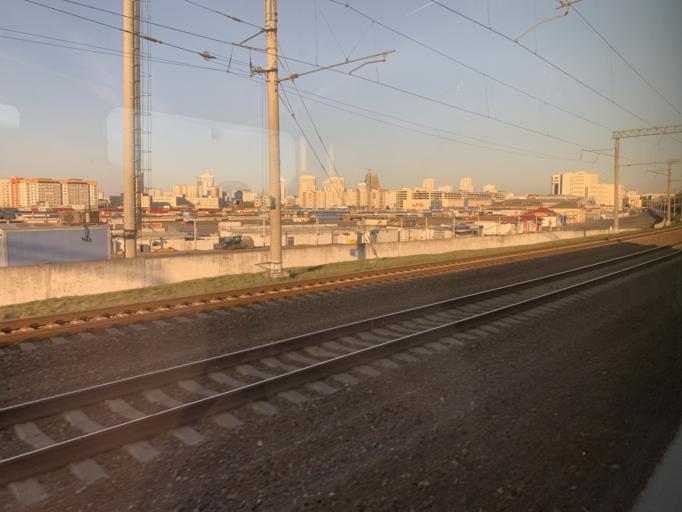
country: BY
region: Minsk
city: Zhdanovichy
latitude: 53.9344
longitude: 27.4475
